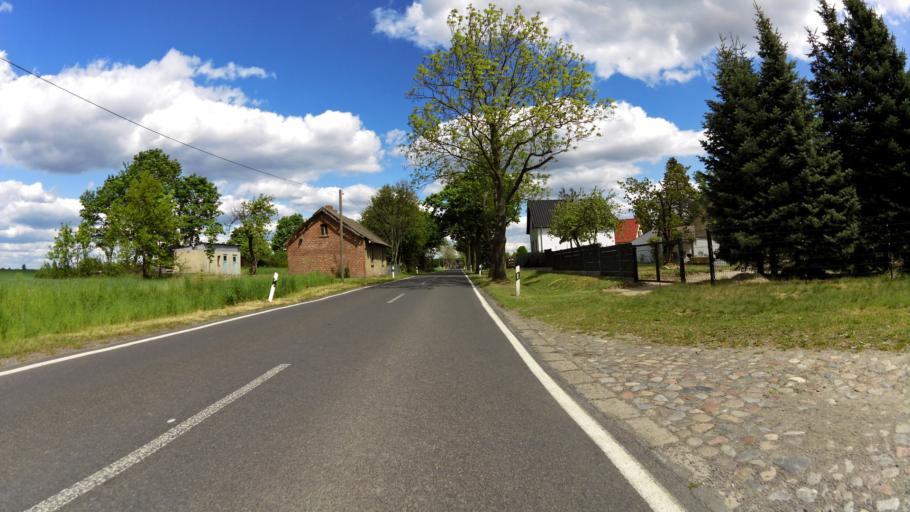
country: DE
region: Brandenburg
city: Diensdorf-Radlow
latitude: 52.1940
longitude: 14.1025
